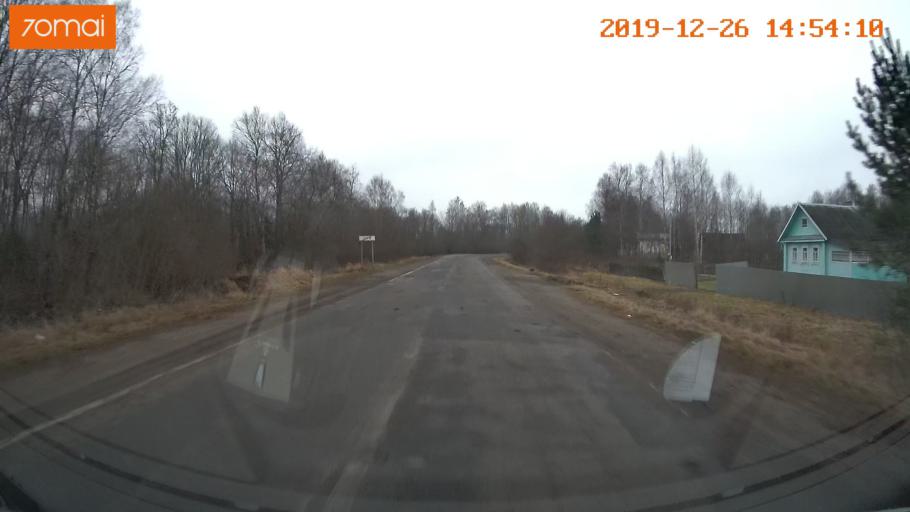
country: RU
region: Jaroslavl
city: Rybinsk
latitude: 58.3093
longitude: 38.8860
